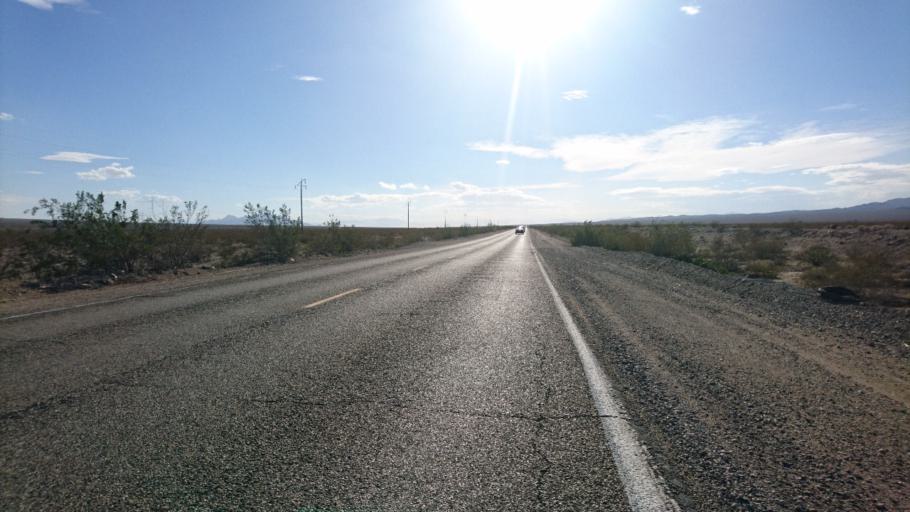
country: US
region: California
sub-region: San Bernardino County
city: Needles
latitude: 34.7112
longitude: -115.2829
